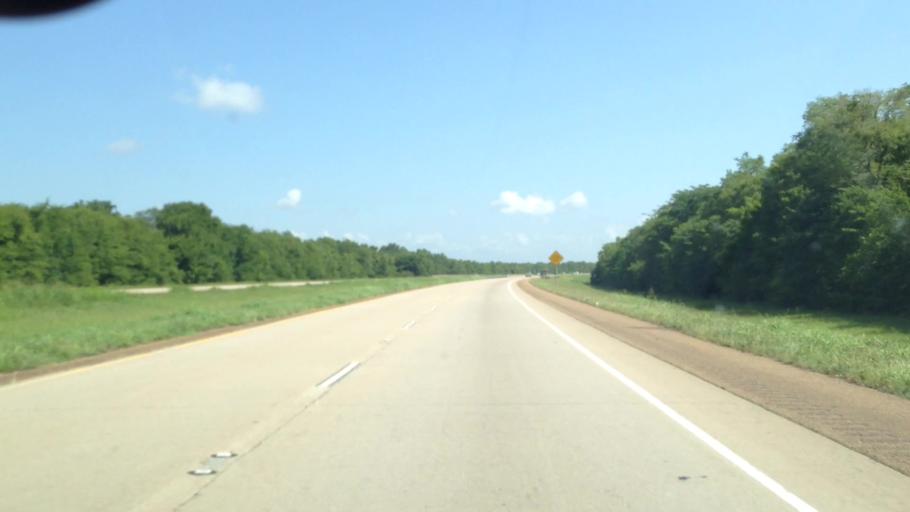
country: US
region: Louisiana
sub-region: Rapides Parish
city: Woodworth
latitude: 31.1946
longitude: -92.4739
